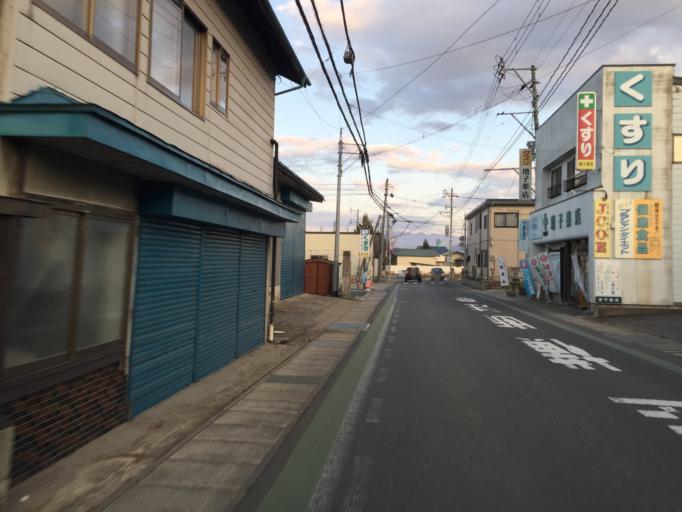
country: JP
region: Yamagata
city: Yonezawa
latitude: 37.9128
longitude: 140.0745
